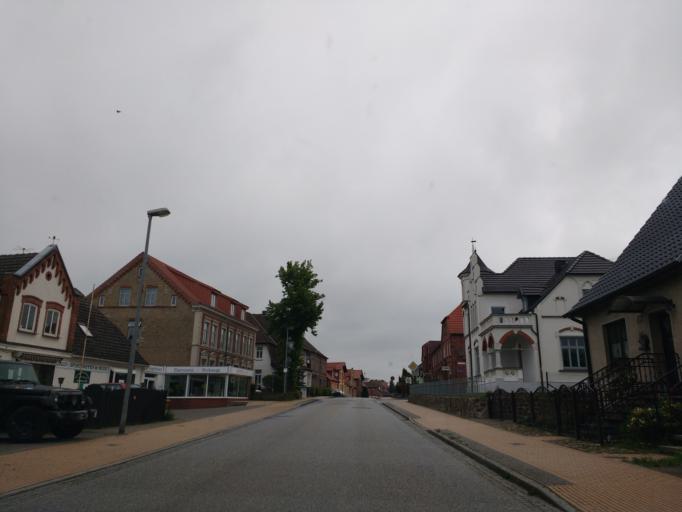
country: DE
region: Mecklenburg-Vorpommern
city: Neukloster
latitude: 53.8647
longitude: 11.6784
